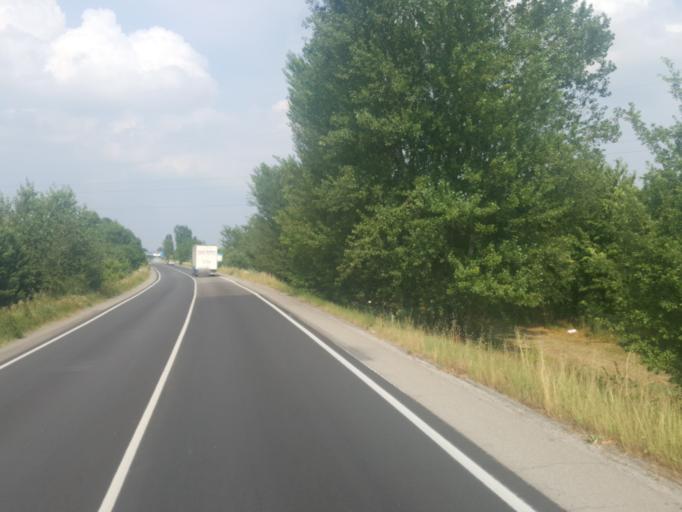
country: IT
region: Emilia-Romagna
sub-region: Provincia di Modena
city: Castelfranco Emilia
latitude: 44.5810
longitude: 11.0698
